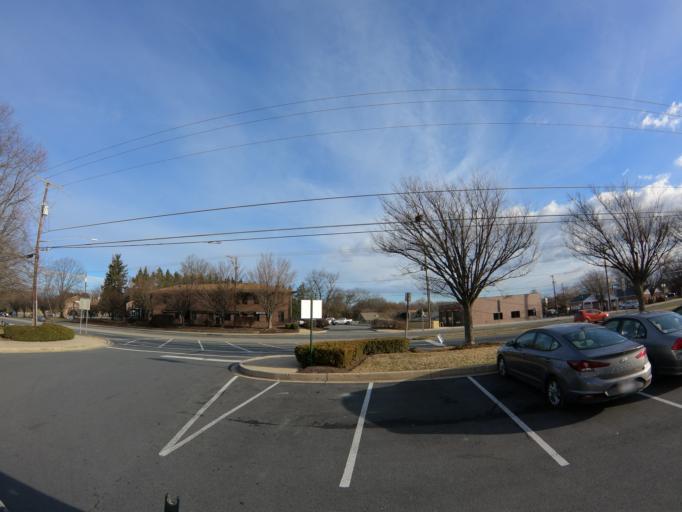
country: US
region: Maryland
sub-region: Montgomery County
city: Olney
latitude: 39.1536
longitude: -77.0683
